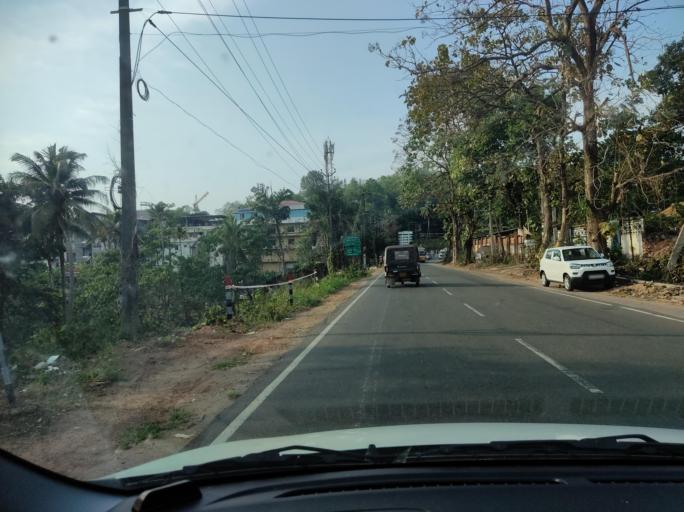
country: IN
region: Kerala
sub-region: Kottayam
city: Kottayam
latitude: 9.6320
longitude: 76.5245
